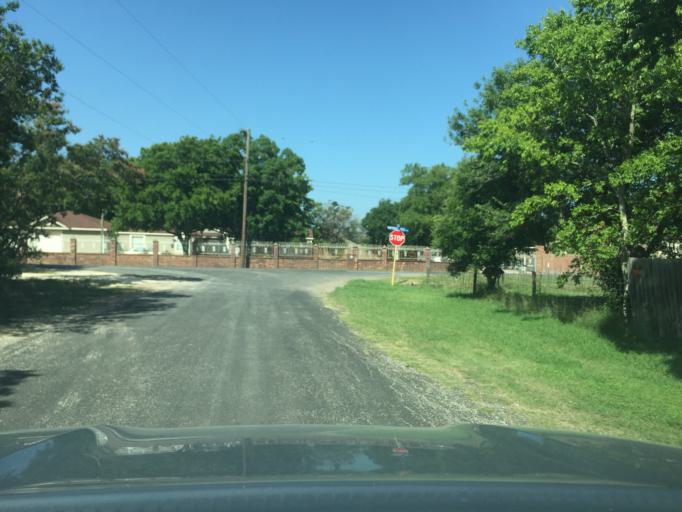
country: US
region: Texas
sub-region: Bexar County
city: Timberwood Park
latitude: 29.7044
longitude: -98.4789
